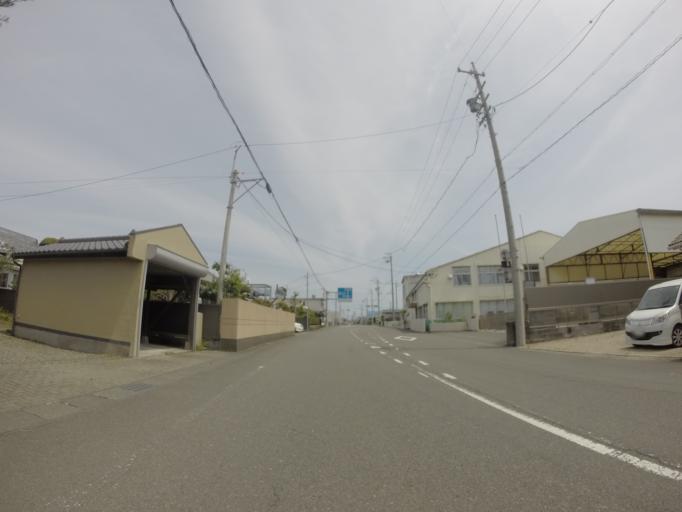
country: JP
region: Shizuoka
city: Yaizu
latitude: 34.7905
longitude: 138.3041
